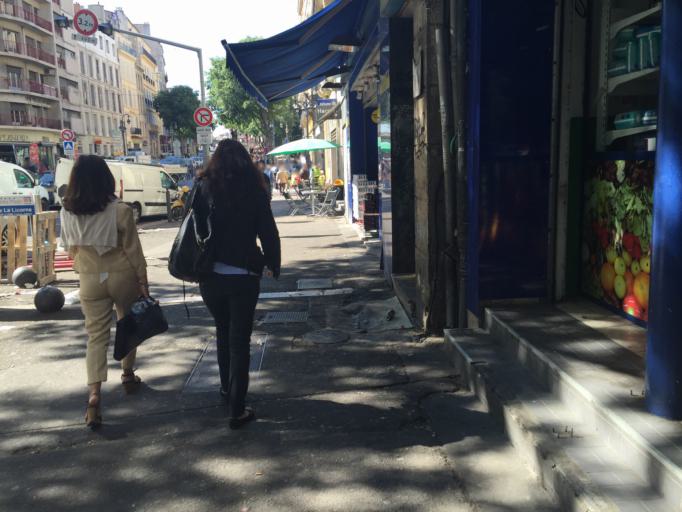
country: FR
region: Provence-Alpes-Cote d'Azur
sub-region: Departement des Bouches-du-Rhone
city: Marseille
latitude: 43.2980
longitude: 5.3811
